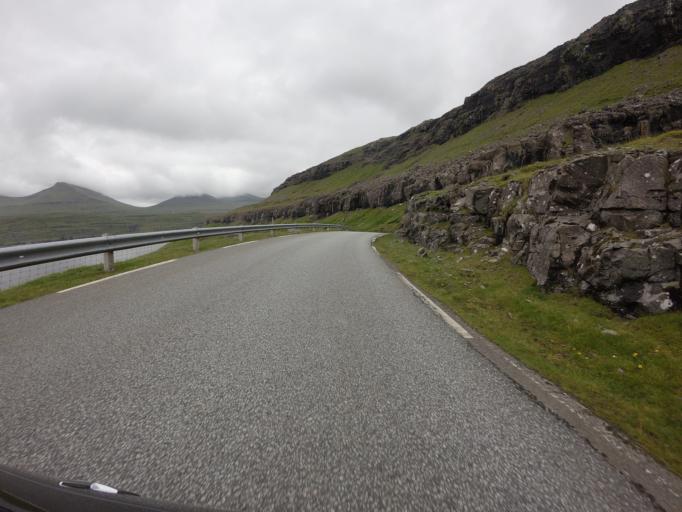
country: FO
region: Eysturoy
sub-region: Eidi
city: Eidi
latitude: 62.2935
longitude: -7.1223
